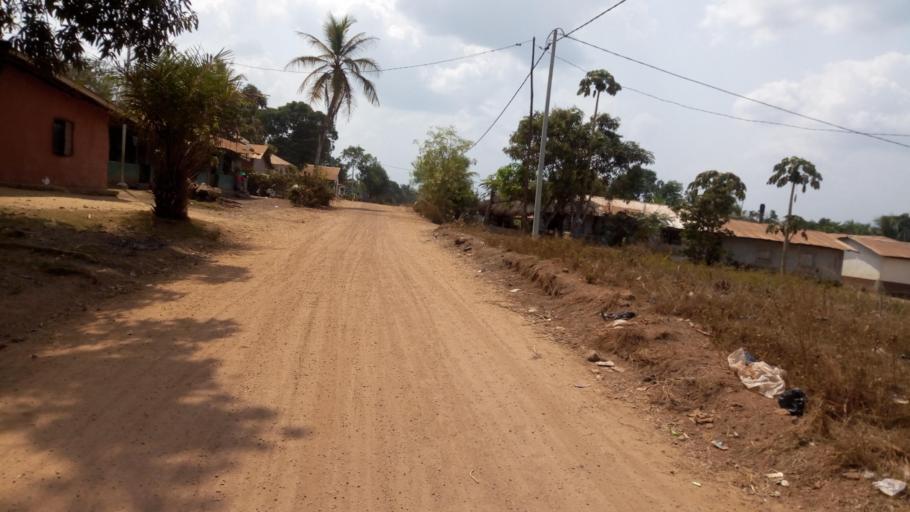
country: SL
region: Southern Province
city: Mogbwemo
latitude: 7.7949
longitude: -12.2982
